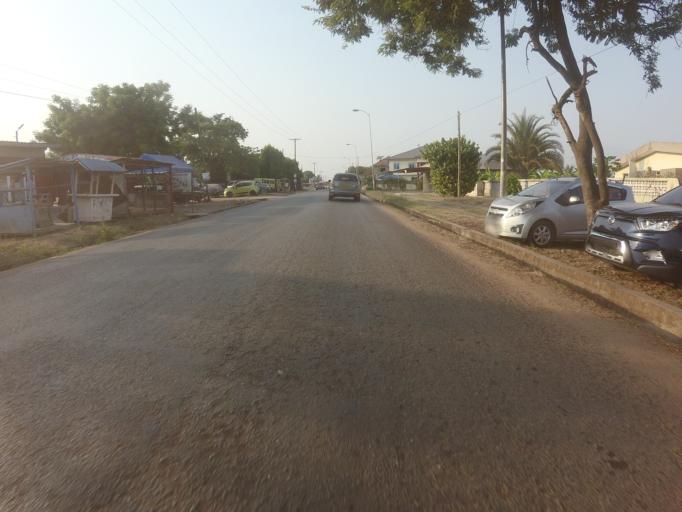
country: GH
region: Greater Accra
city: Nungua
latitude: 5.6190
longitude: -0.0542
